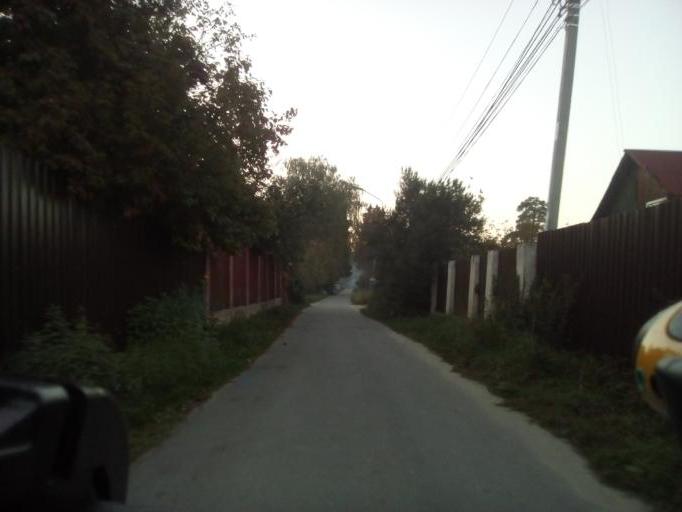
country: RU
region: Moskovskaya
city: Kratovo
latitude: 55.6014
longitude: 38.1816
